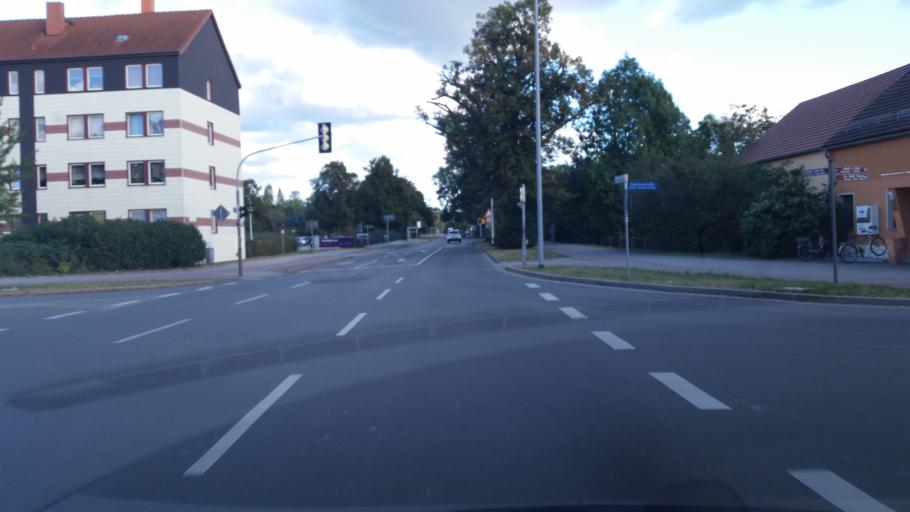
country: DE
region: Saxony
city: Hoyerswerda
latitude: 51.4402
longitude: 14.2486
